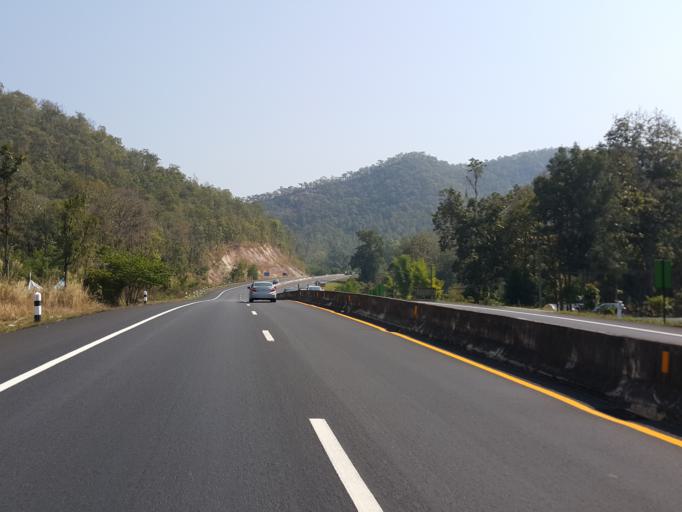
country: TH
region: Chiang Mai
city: San Sai
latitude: 18.8931
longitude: 99.1717
